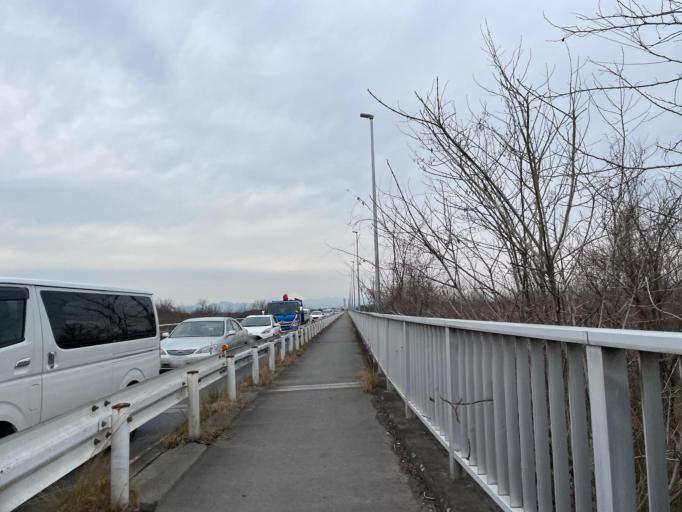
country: JP
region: Gunma
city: Fujioka
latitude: 36.2357
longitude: 139.1000
